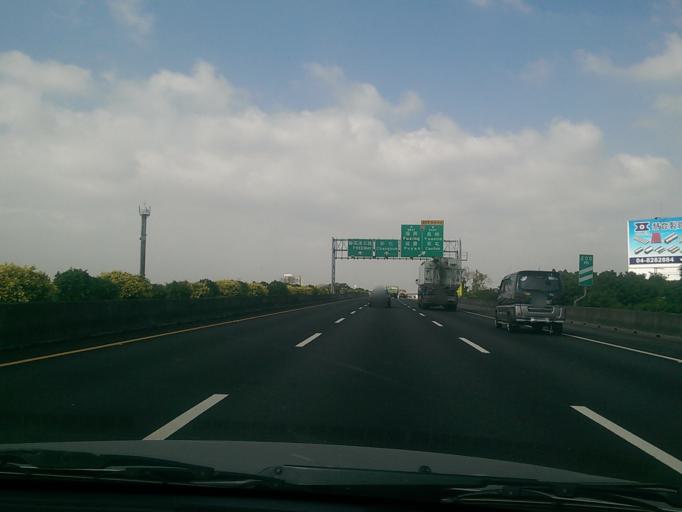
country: TW
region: Taiwan
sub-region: Changhua
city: Chang-hua
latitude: 23.9734
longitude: 120.5062
